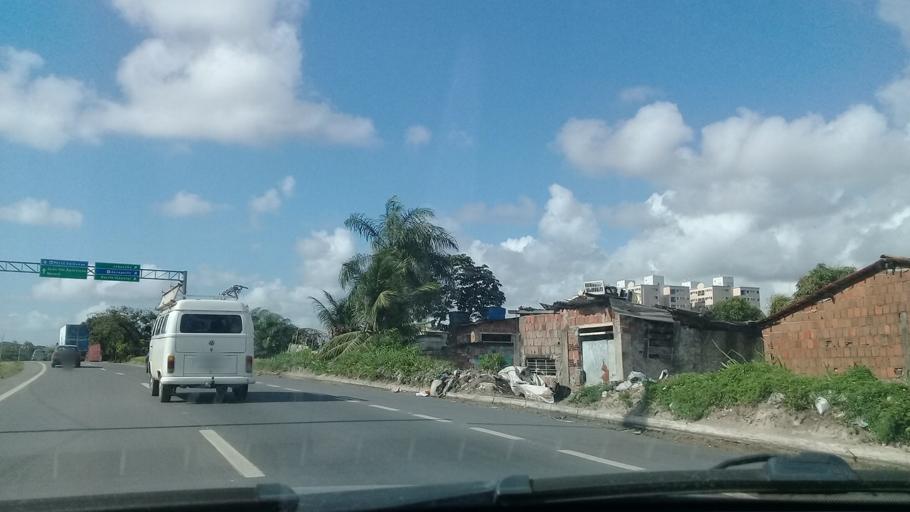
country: BR
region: Pernambuco
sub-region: Jaboatao Dos Guararapes
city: Jaboatao dos Guararapes
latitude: -8.0883
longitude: -34.9469
